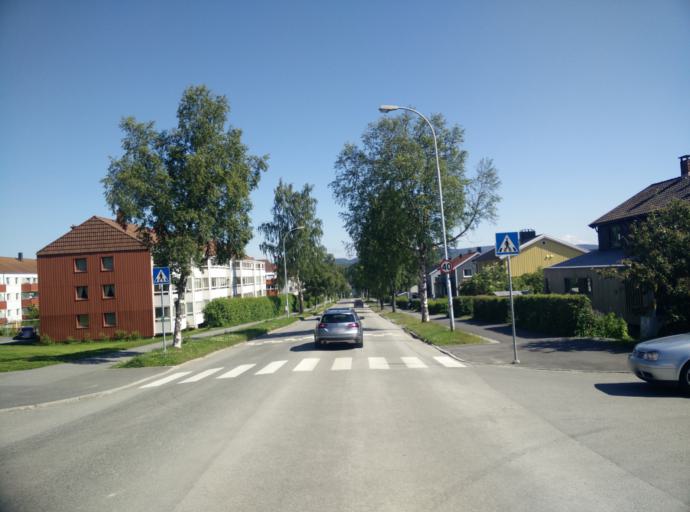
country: NO
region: Sor-Trondelag
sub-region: Trondheim
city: Trondheim
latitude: 63.4171
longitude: 10.3565
